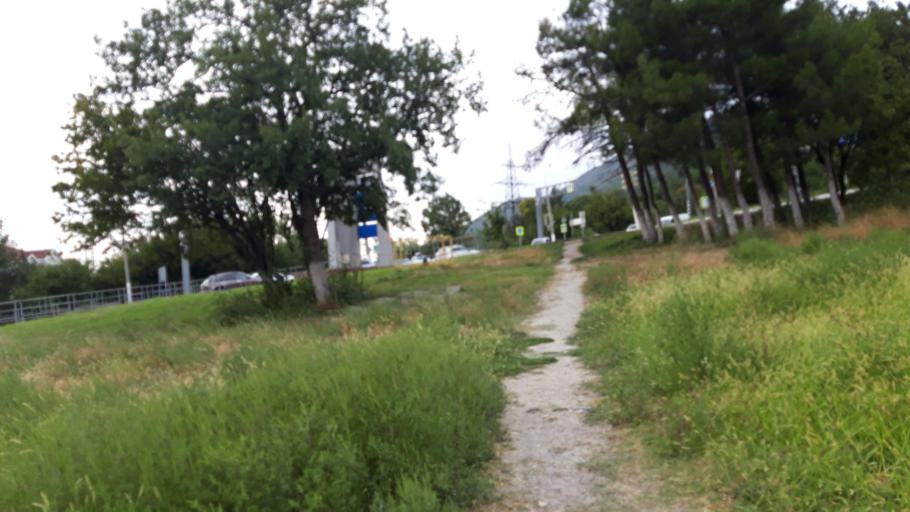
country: RU
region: Krasnodarskiy
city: Gelendzhik
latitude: 44.5728
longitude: 38.0914
